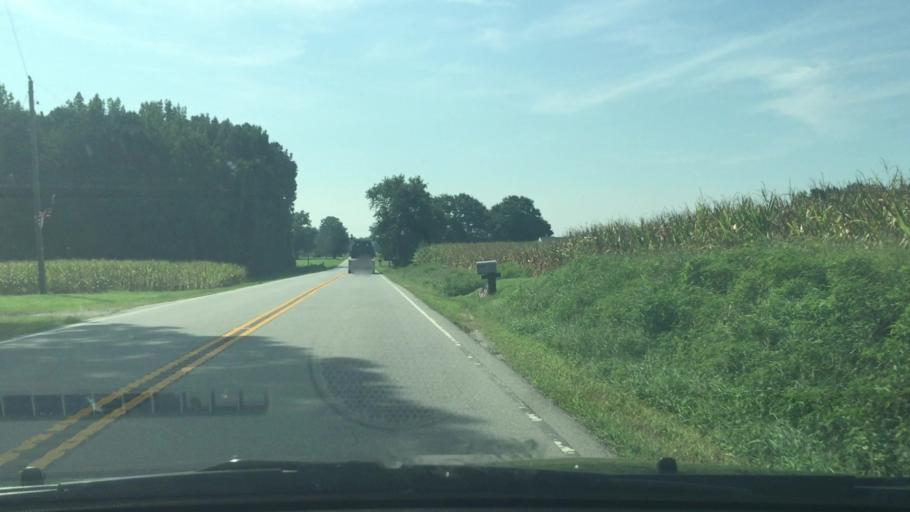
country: US
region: Virginia
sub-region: Sussex County
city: Sussex
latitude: 36.8815
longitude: -77.1524
